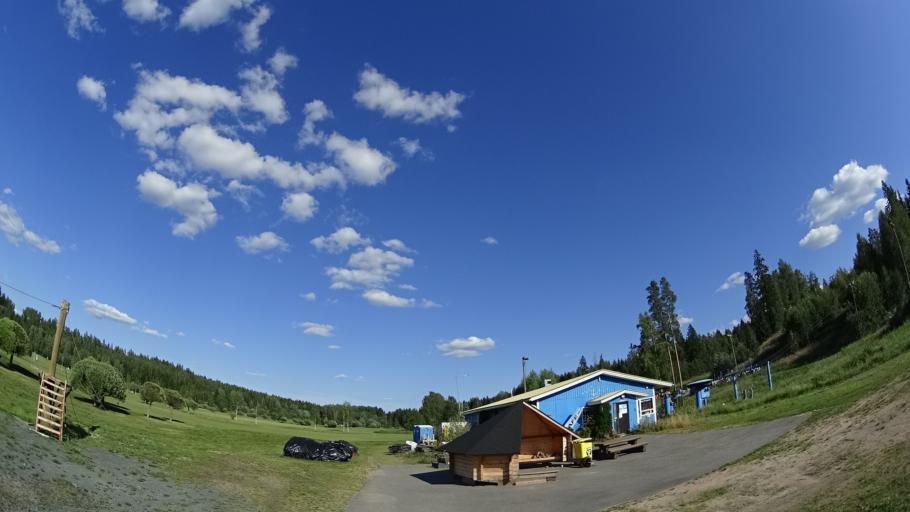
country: FI
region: Uusimaa
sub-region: Helsinki
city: Vihti
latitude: 60.3800
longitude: 24.3686
